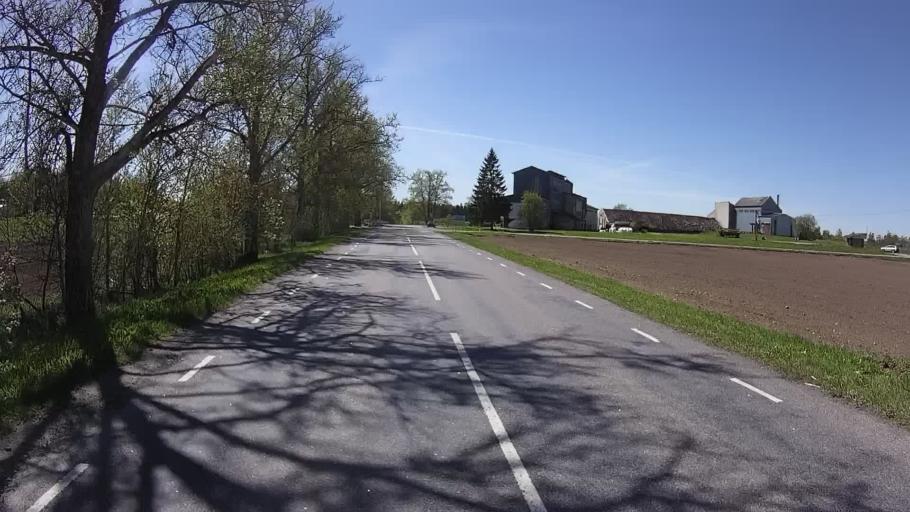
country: EE
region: Raplamaa
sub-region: Kehtna vald
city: Kehtna
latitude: 59.0466
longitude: 25.1177
